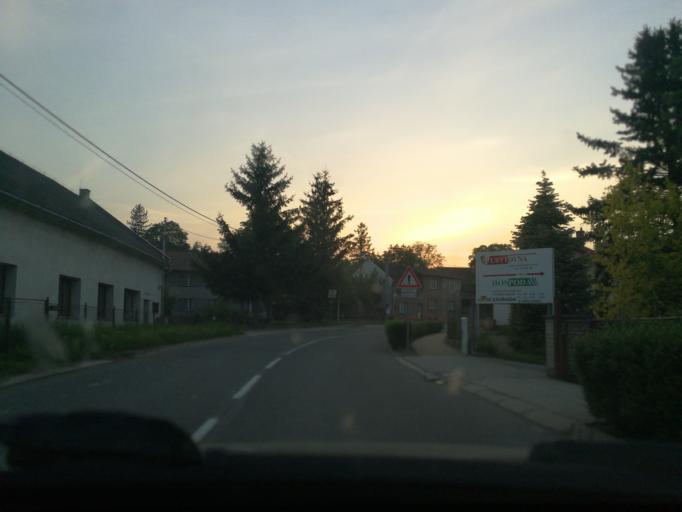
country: CZ
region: Zlin
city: Tecovice
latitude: 49.2548
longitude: 17.5678
